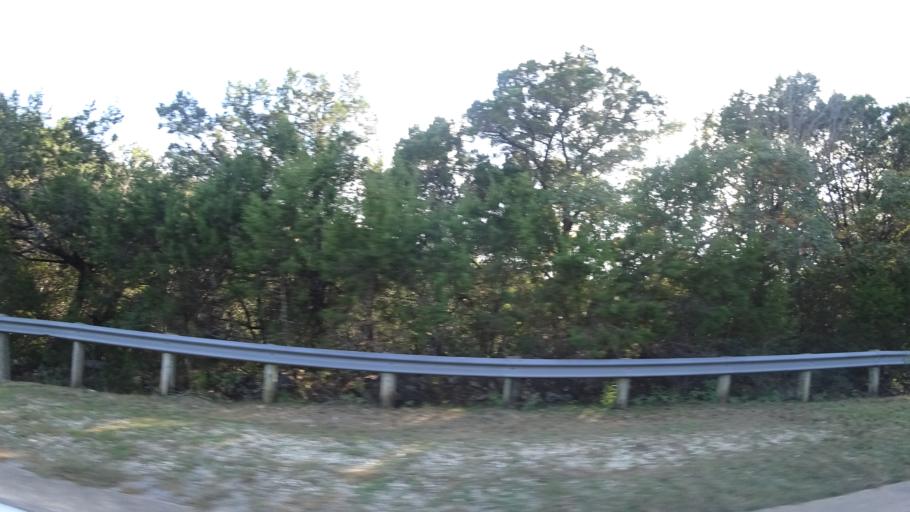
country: US
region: Texas
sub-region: Travis County
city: Barton Creek
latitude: 30.2768
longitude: -97.8685
